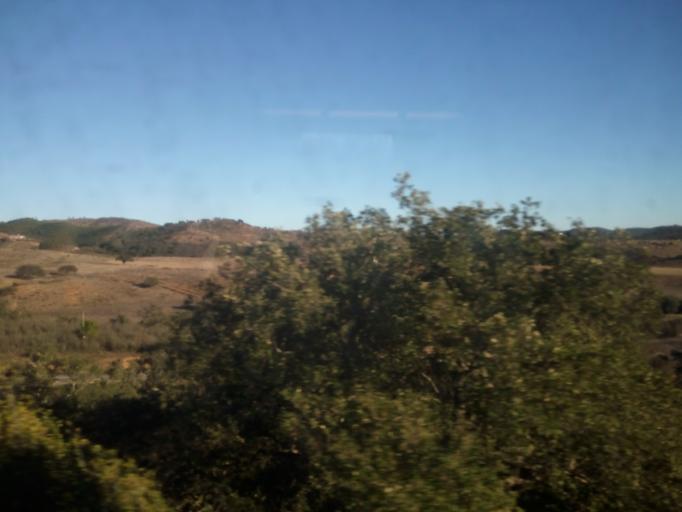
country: PT
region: Beja
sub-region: Odemira
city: Odemira
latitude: 37.5180
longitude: -8.4763
